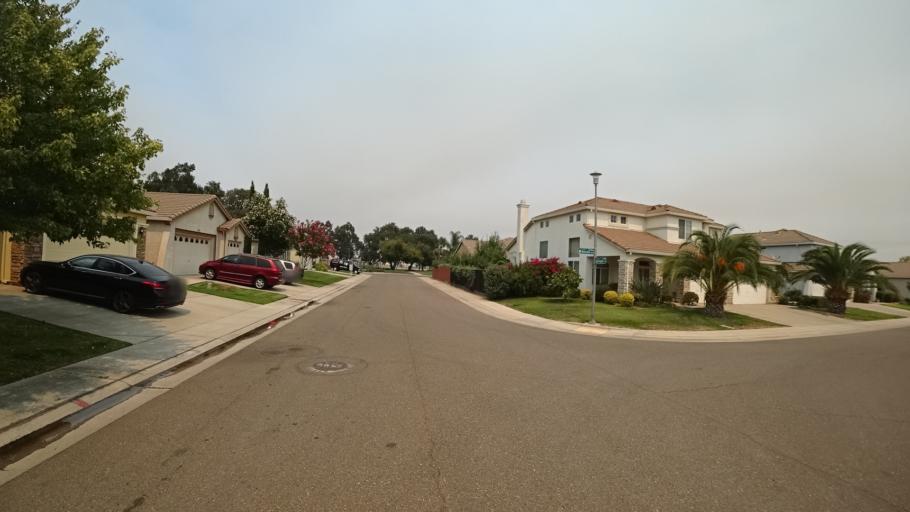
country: US
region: California
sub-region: Sacramento County
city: Laguna
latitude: 38.3959
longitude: -121.4238
